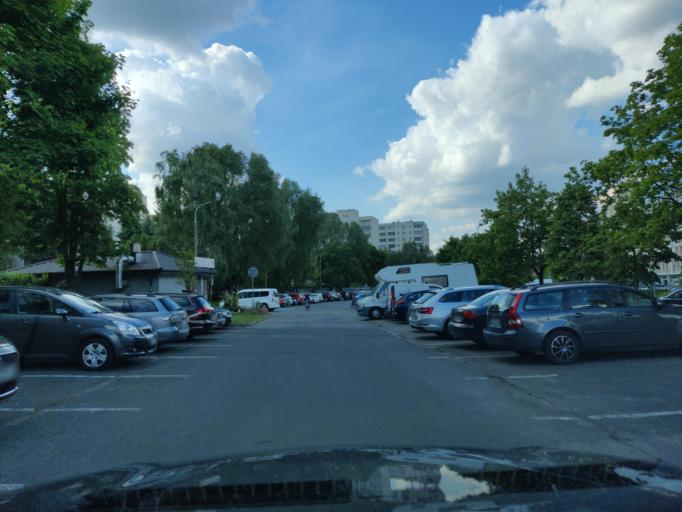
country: PL
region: Masovian Voivodeship
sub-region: Warszawa
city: Ursynow
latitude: 52.1428
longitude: 21.0441
